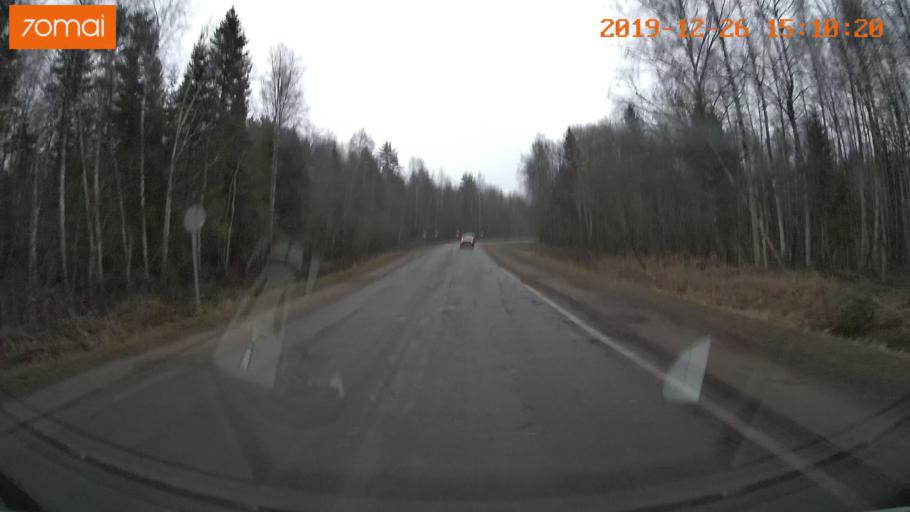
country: RU
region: Jaroslavl
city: Rybinsk
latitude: 58.1411
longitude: 38.8505
